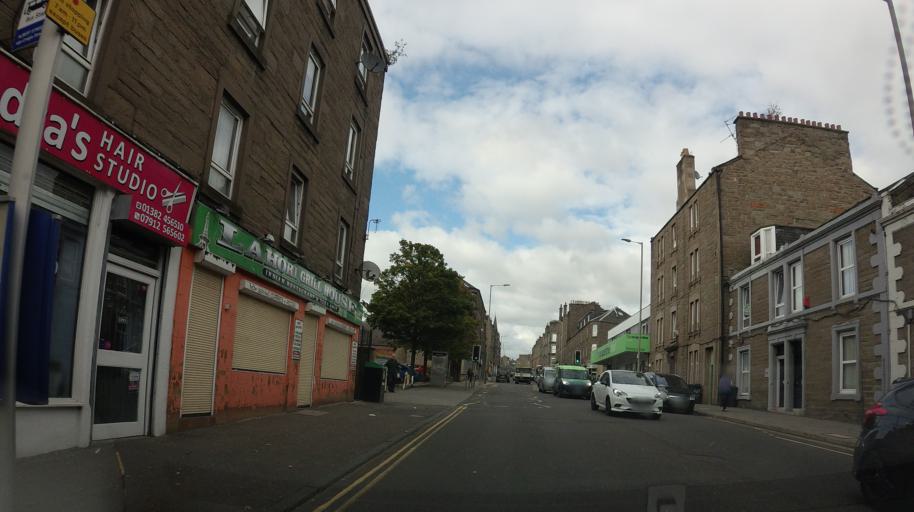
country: GB
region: Scotland
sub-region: Dundee City
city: Dundee
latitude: 56.4697
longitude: -2.9575
